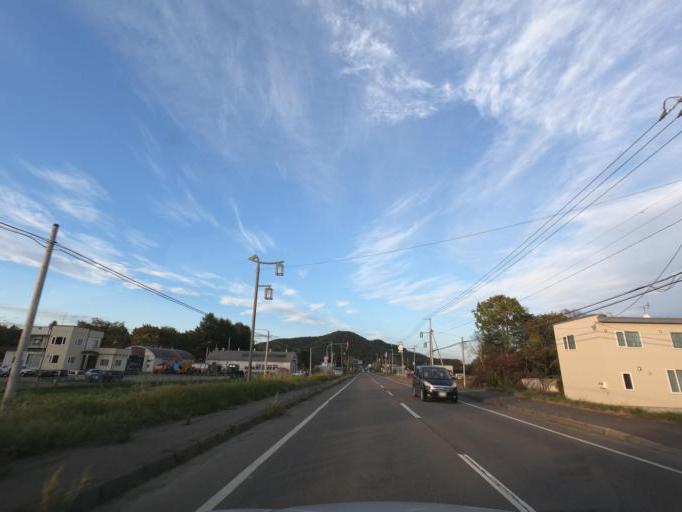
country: JP
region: Hokkaido
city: Obihiro
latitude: 42.5680
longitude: 143.3048
